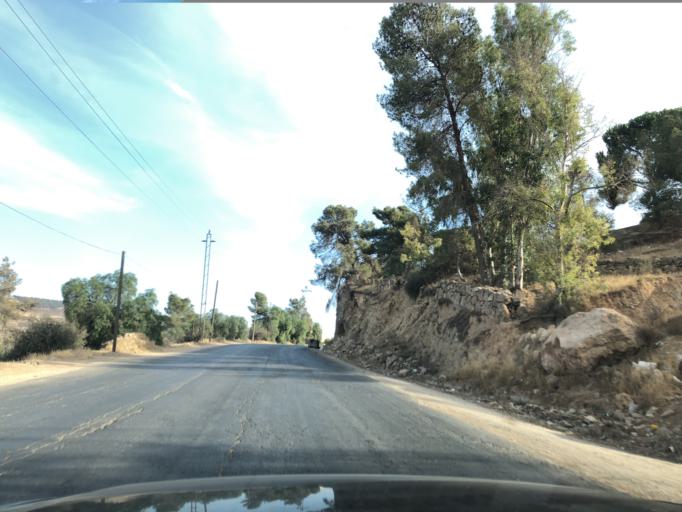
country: JO
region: Jerash
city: Jarash
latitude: 32.2658
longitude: 35.8881
